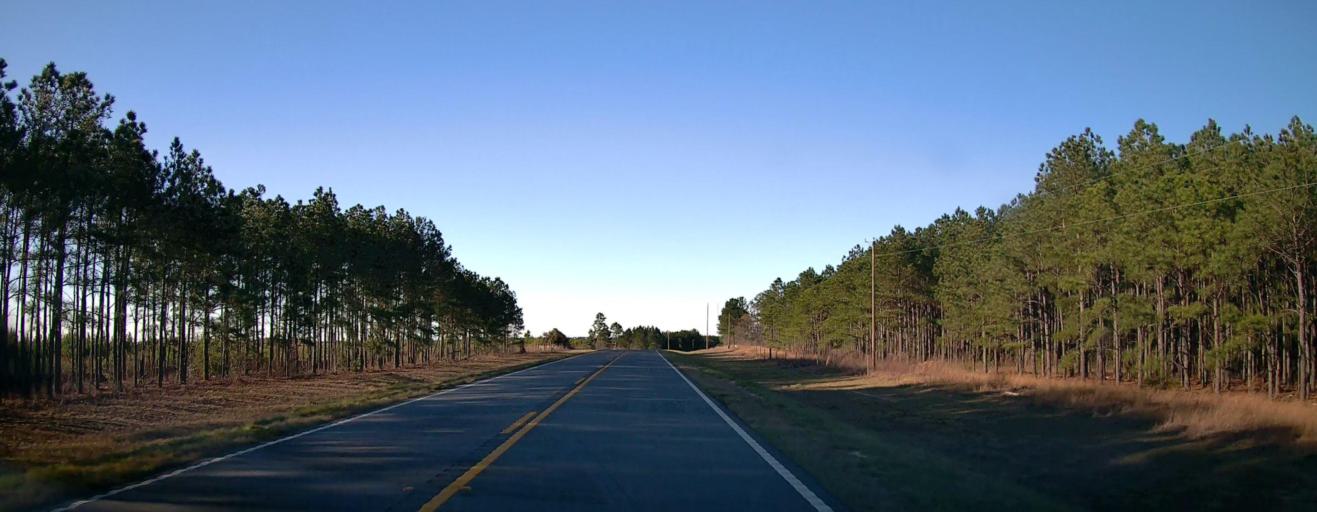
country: US
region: Georgia
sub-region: Talbot County
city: Talbotton
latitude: 32.5519
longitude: -84.4367
